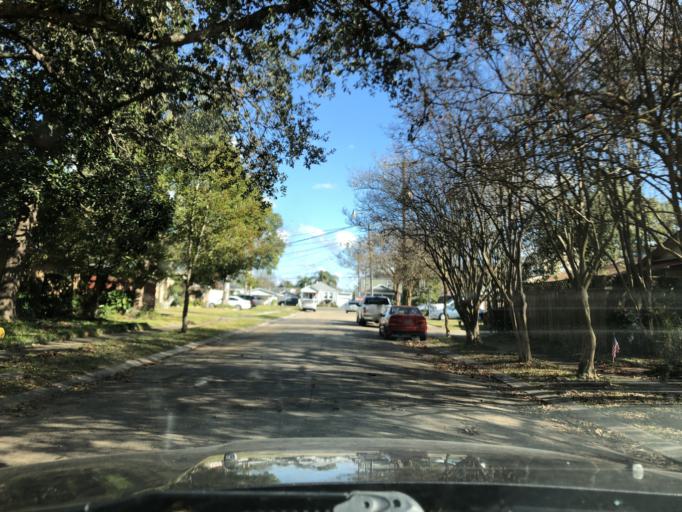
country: US
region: Louisiana
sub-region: Jefferson Parish
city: Metairie
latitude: 29.9862
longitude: -90.1601
